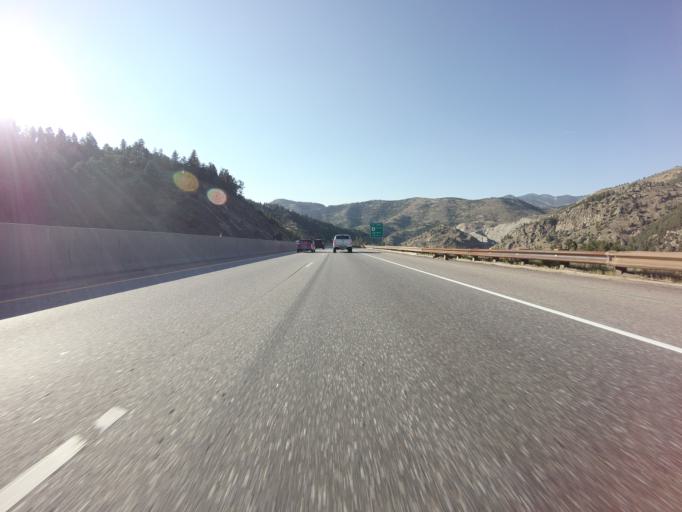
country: US
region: Colorado
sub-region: Clear Creek County
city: Idaho Springs
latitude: 39.7353
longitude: -105.4293
